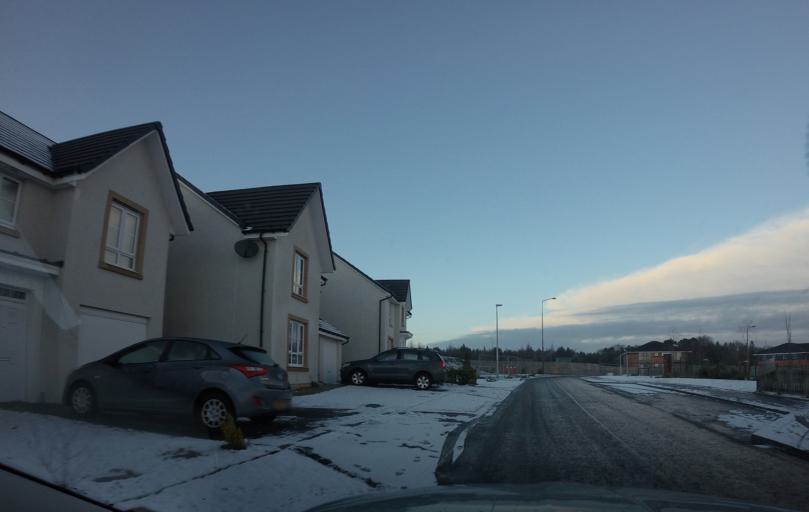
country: GB
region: Scotland
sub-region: West Lothian
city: Livingston
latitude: 55.8890
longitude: -3.5525
